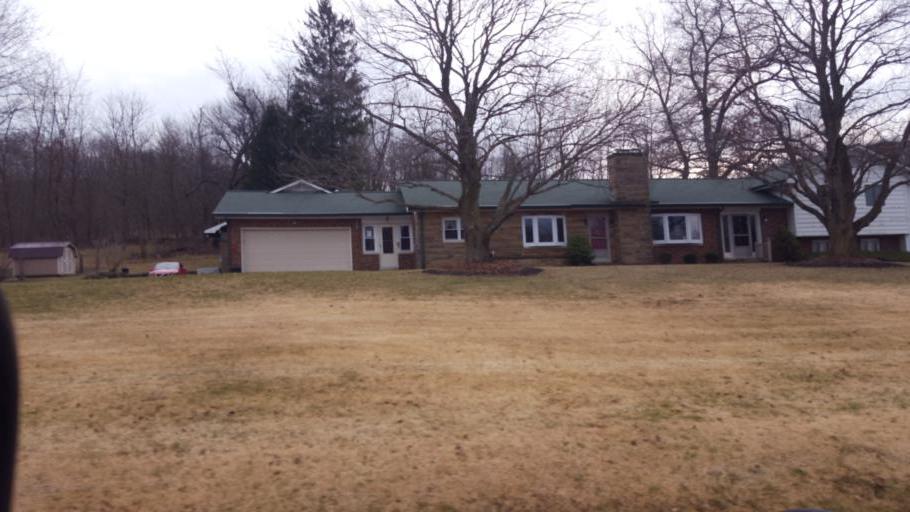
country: US
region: Ohio
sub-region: Knox County
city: Danville
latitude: 40.5352
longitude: -82.2998
